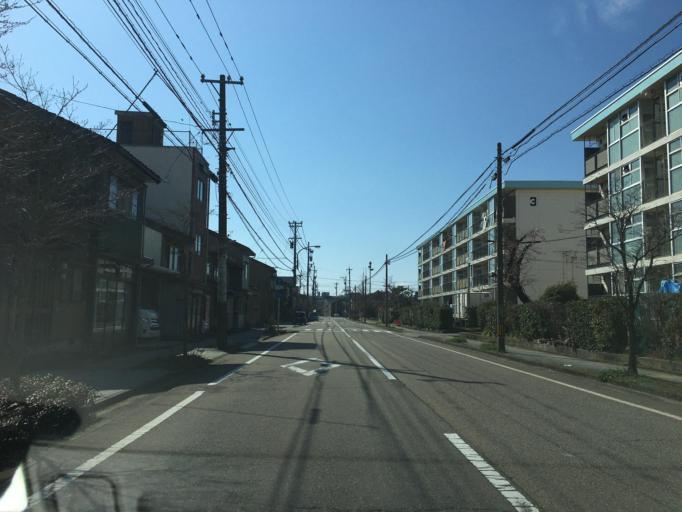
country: JP
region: Toyama
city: Nishishinminato
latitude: 36.7788
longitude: 137.0950
